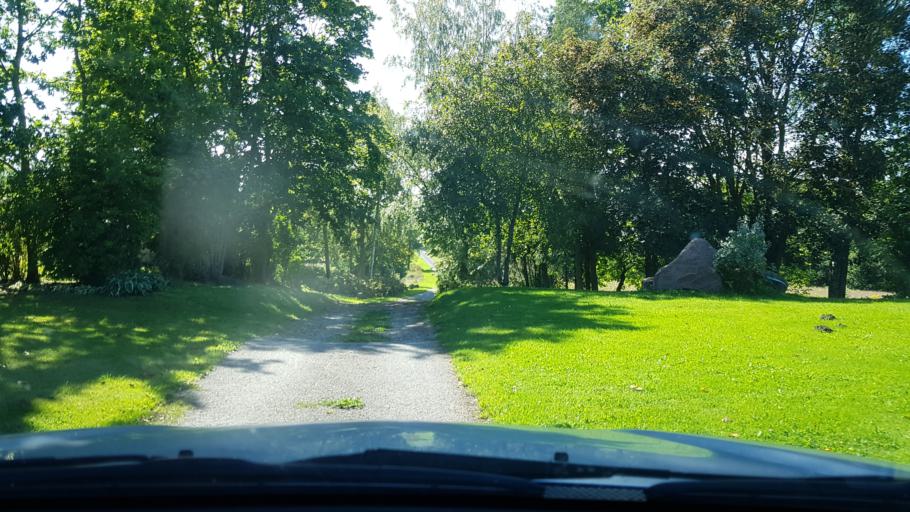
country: EE
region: Ida-Virumaa
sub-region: Sillamaee linn
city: Sillamae
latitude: 59.3908
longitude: 27.8155
